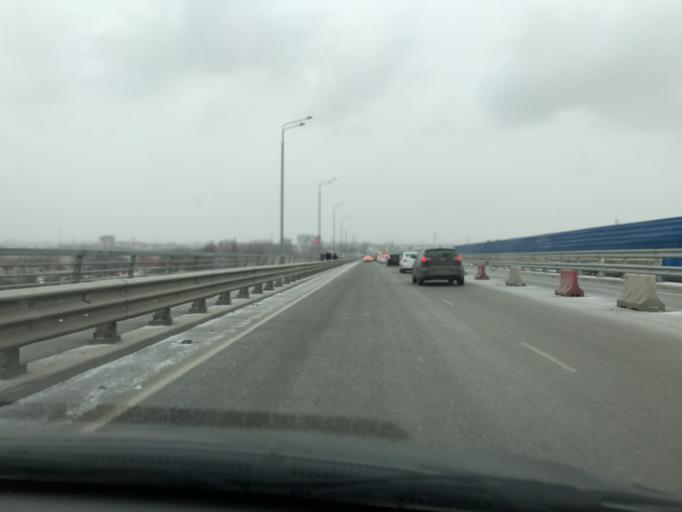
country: RU
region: Rostov
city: Rostov-na-Donu
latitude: 47.2132
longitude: 39.7231
